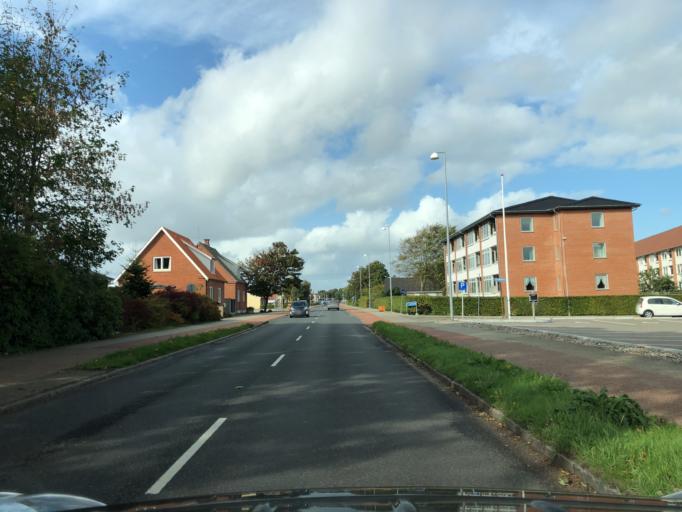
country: DK
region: Central Jutland
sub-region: Holstebro Kommune
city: Holstebro
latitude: 56.3717
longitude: 8.6164
